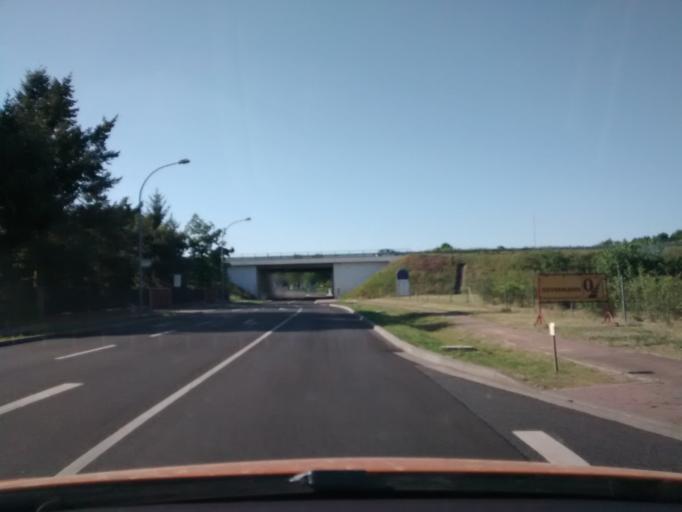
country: DE
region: Brandenburg
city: Langewahl
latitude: 52.3337
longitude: 14.0756
